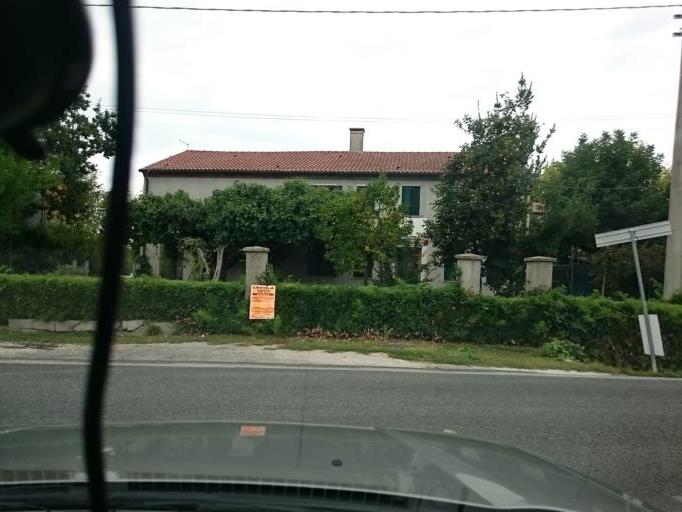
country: IT
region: Veneto
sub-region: Provincia di Padova
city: Mestrino
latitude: 45.4257
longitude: 11.7536
